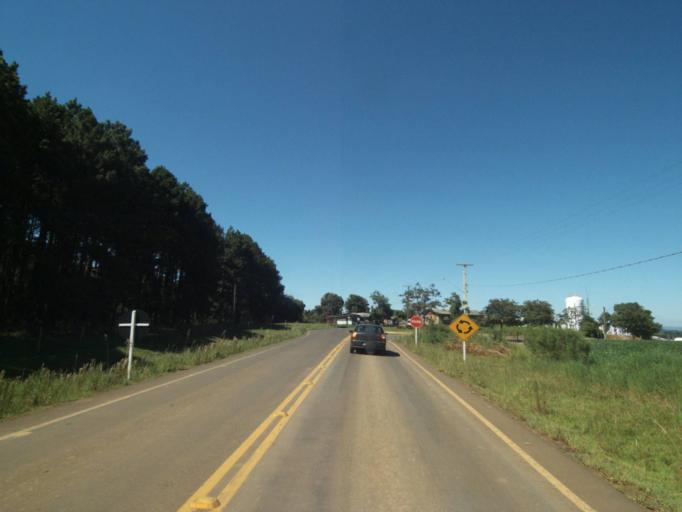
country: BR
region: Parana
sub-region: Pinhao
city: Pinhao
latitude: -25.8343
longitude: -52.0224
